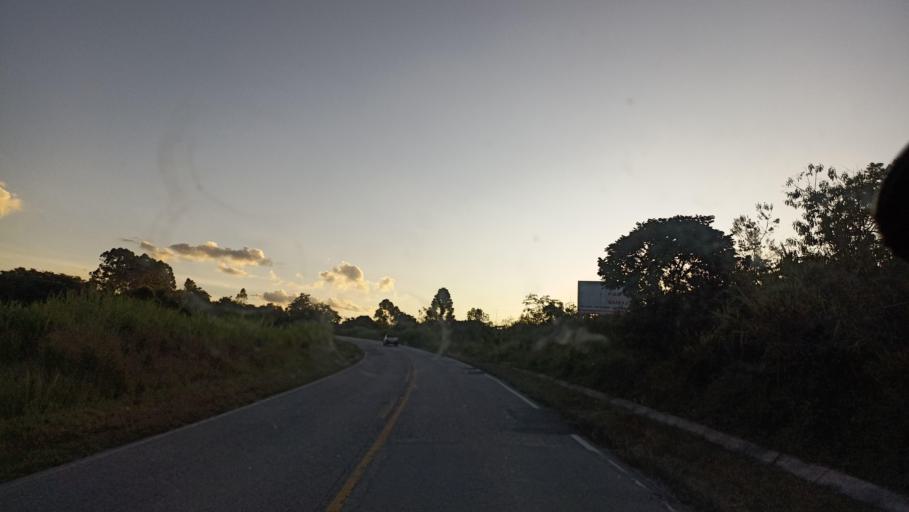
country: BR
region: Minas Gerais
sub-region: Sao Joao Del Rei
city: Sao Joao del Rei
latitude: -21.2353
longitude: -44.3934
